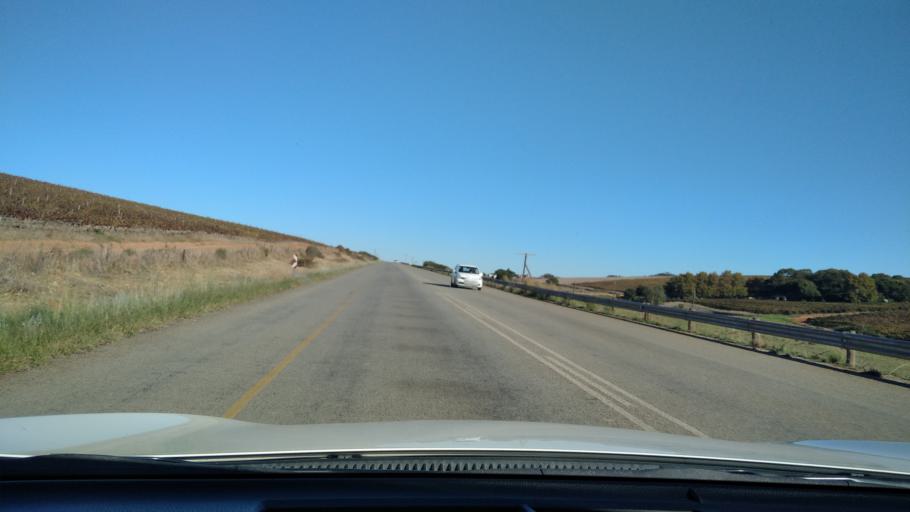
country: ZA
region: Western Cape
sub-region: West Coast District Municipality
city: Malmesbury
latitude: -33.3986
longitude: 18.6871
